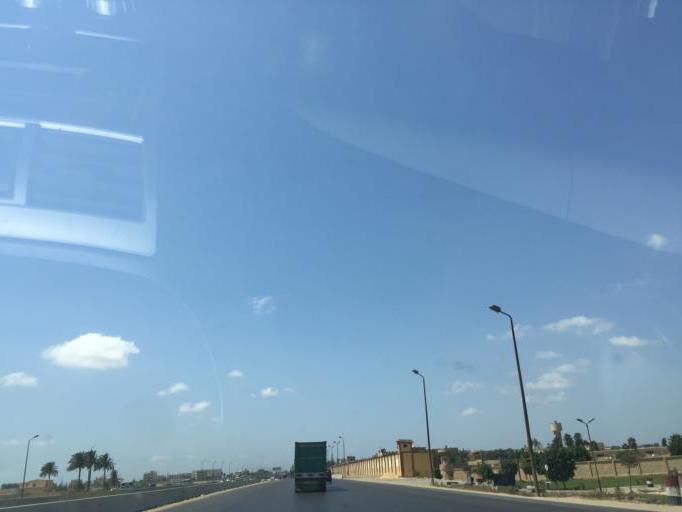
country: EG
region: Alexandria
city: Alexandria
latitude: 30.9950
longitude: 29.8098
